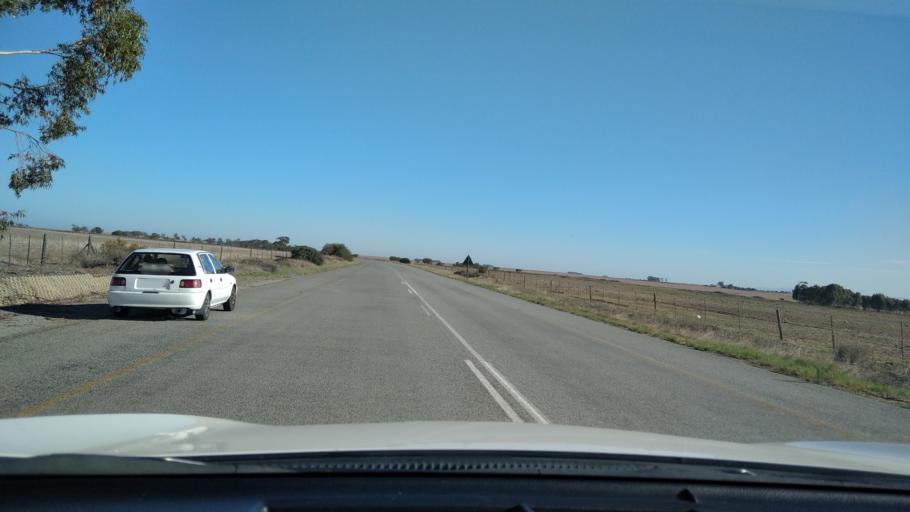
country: ZA
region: Western Cape
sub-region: West Coast District Municipality
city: Moorreesburg
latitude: -33.2605
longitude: 18.5928
